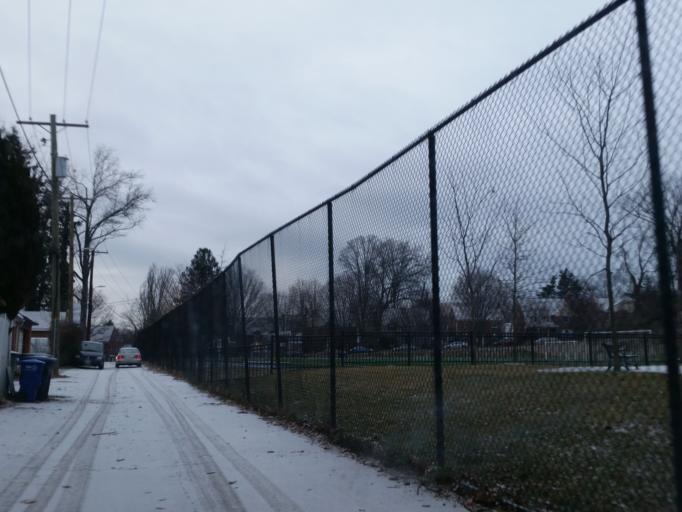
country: US
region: Maryland
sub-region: Montgomery County
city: Silver Spring
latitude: 38.9843
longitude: -77.0355
